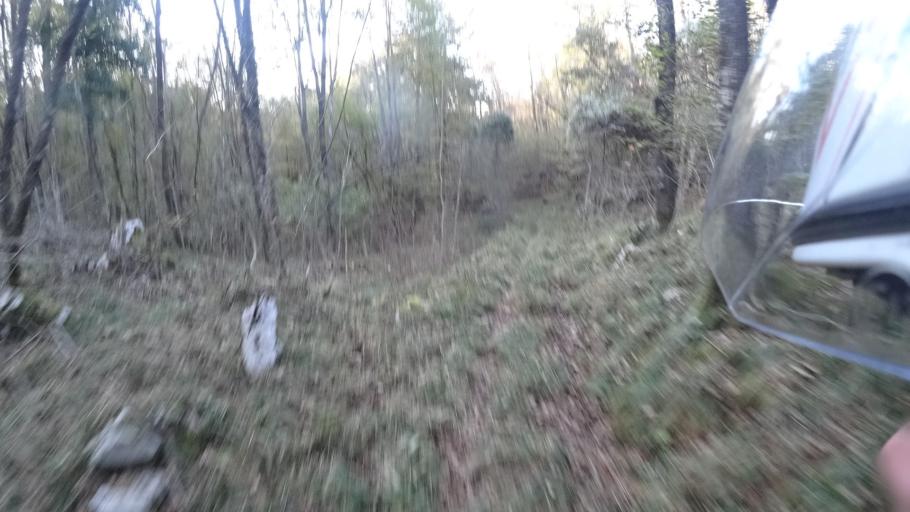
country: HR
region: Primorsko-Goranska
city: Kastav
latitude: 45.4017
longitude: 14.3185
